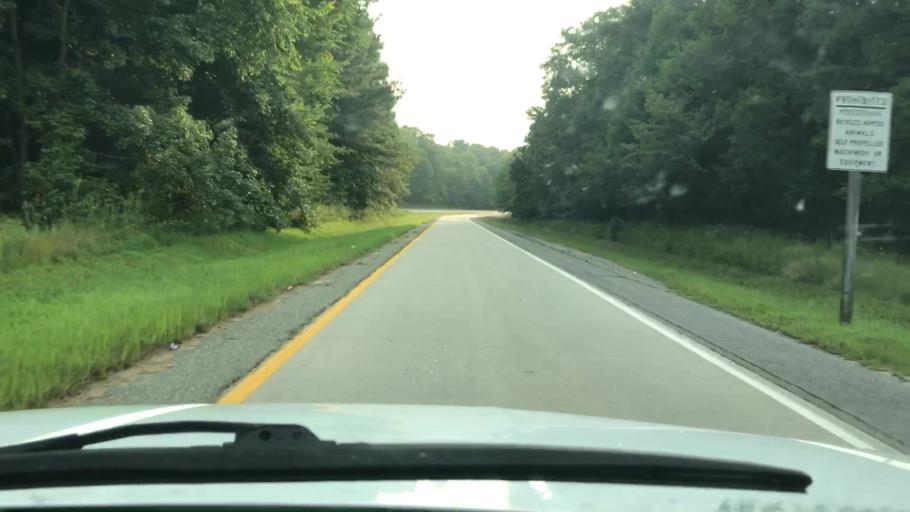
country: US
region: Virginia
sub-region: Chesterfield County
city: Chesterfield
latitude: 37.4103
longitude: -77.5675
